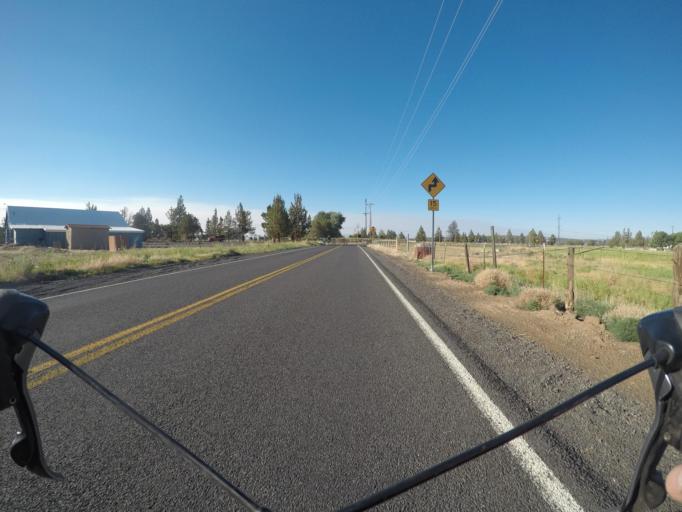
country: US
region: Oregon
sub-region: Deschutes County
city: Redmond
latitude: 44.2117
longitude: -121.2436
